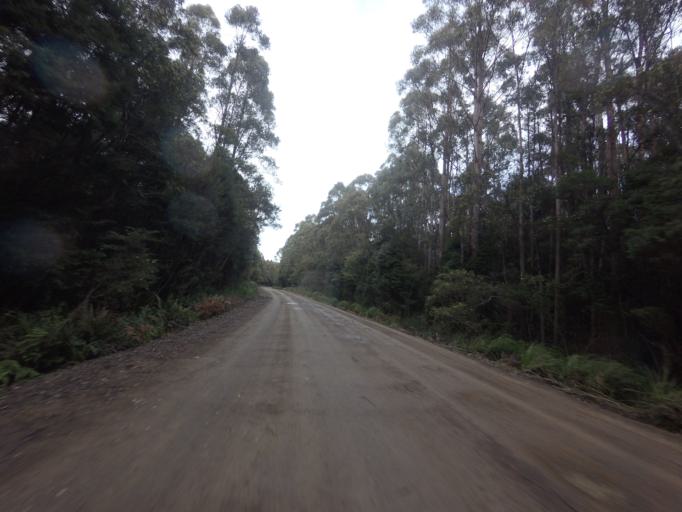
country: AU
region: Tasmania
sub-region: Huon Valley
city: Geeveston
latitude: -43.5181
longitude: 146.8845
